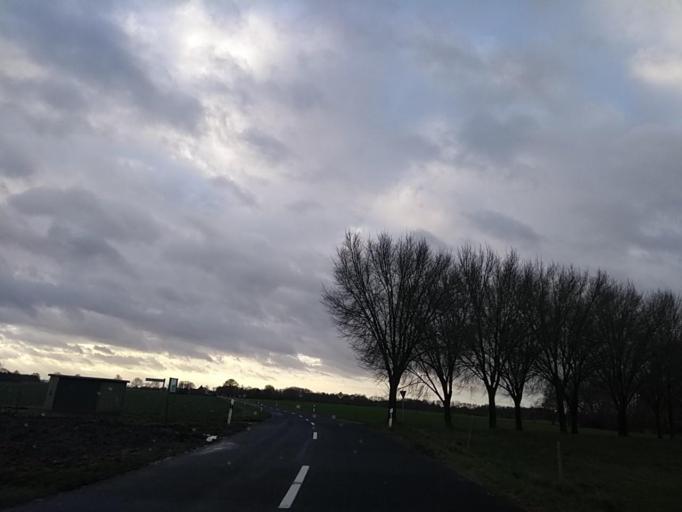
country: DE
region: Lower Saxony
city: Bunde
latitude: 53.1938
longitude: 7.2163
